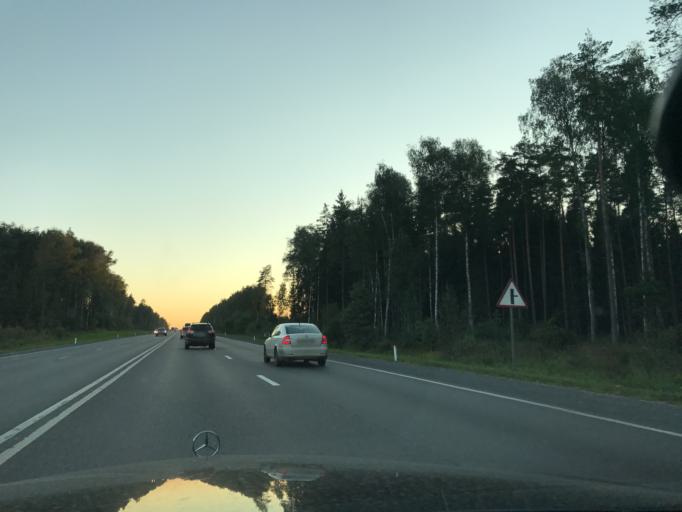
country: RU
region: Vladimir
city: Pokrov
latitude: 55.9272
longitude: 39.3086
